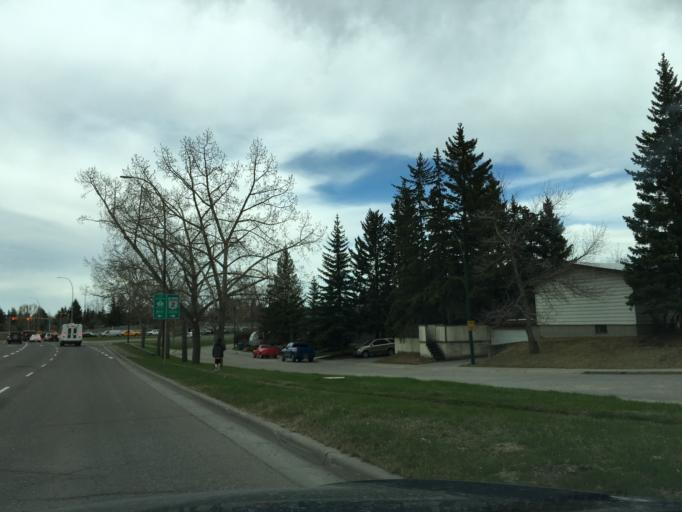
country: CA
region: Alberta
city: Calgary
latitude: 50.9613
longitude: -114.0977
